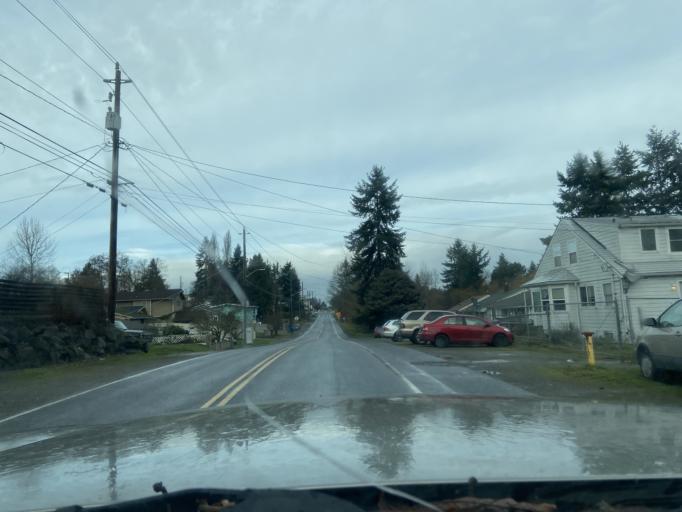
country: US
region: Washington
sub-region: King County
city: White Center
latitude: 47.5086
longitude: -122.3448
